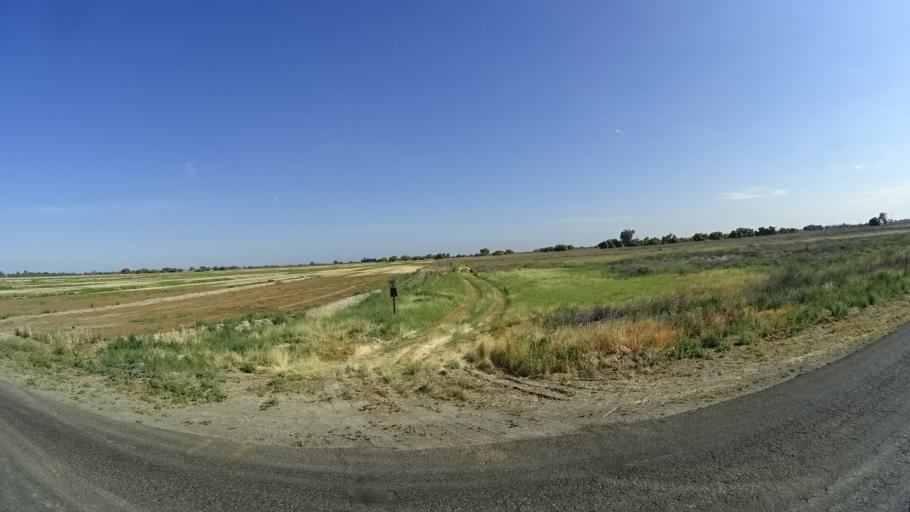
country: US
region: California
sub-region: Kings County
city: Lemoore
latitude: 36.2256
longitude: -119.7357
